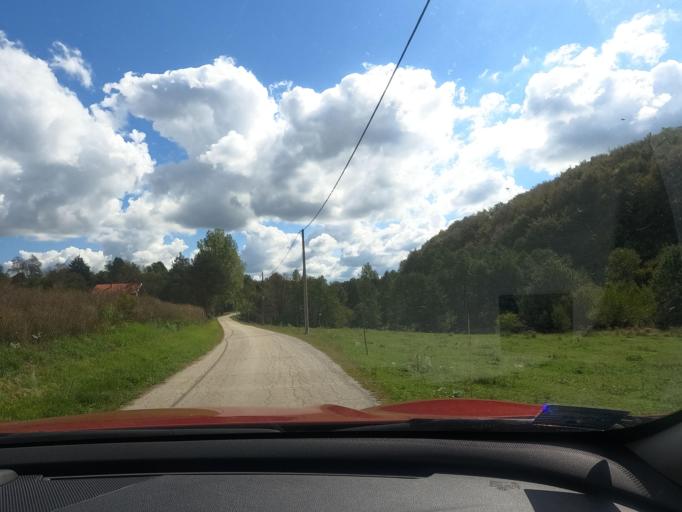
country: BA
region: Federation of Bosnia and Herzegovina
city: Velika Kladusa
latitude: 45.2331
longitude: 15.7670
